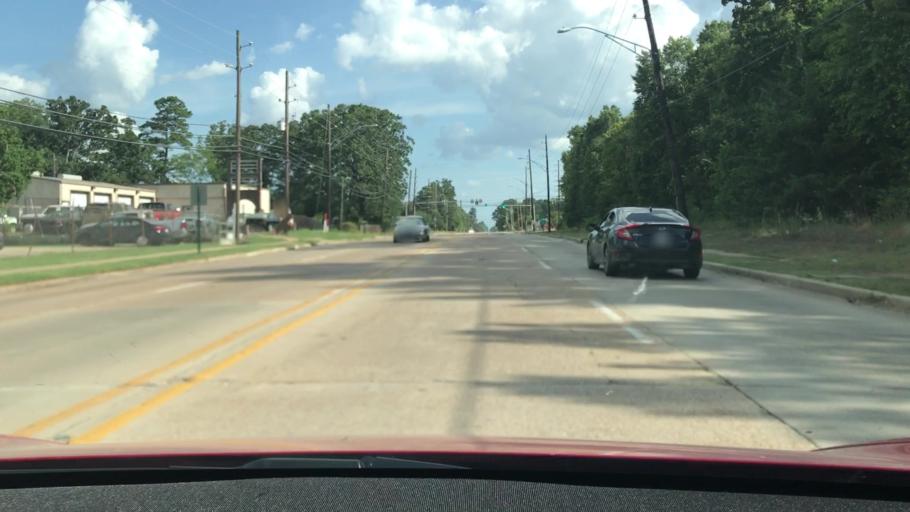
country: US
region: Louisiana
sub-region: Bossier Parish
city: Bossier City
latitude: 32.4147
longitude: -93.7632
